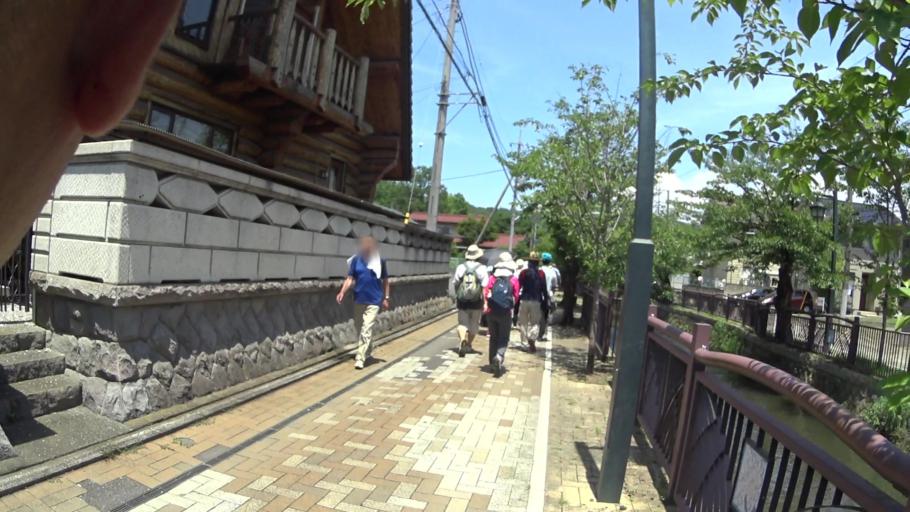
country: JP
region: Gunma
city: Ota
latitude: 36.3006
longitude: 139.3697
